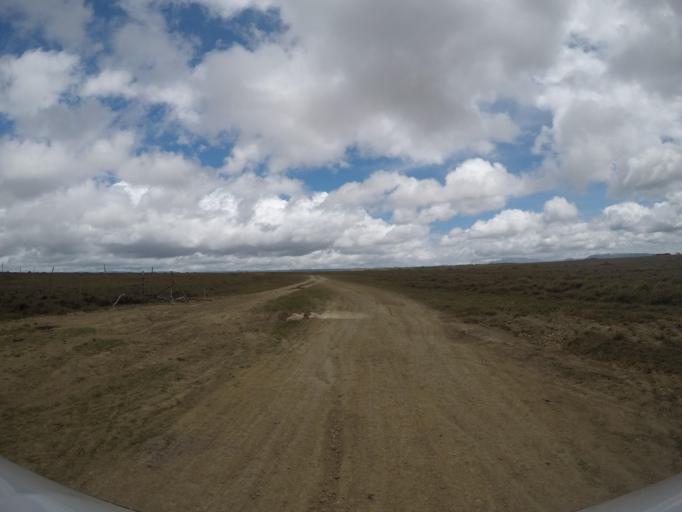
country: TL
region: Lautem
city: Lospalos
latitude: -8.4503
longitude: 126.9860
